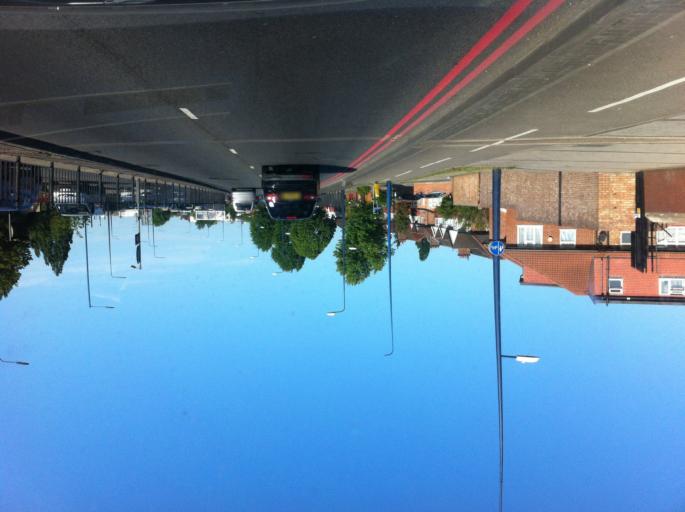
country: GB
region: England
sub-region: Greater London
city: Acton
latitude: 51.5158
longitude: -0.2587
